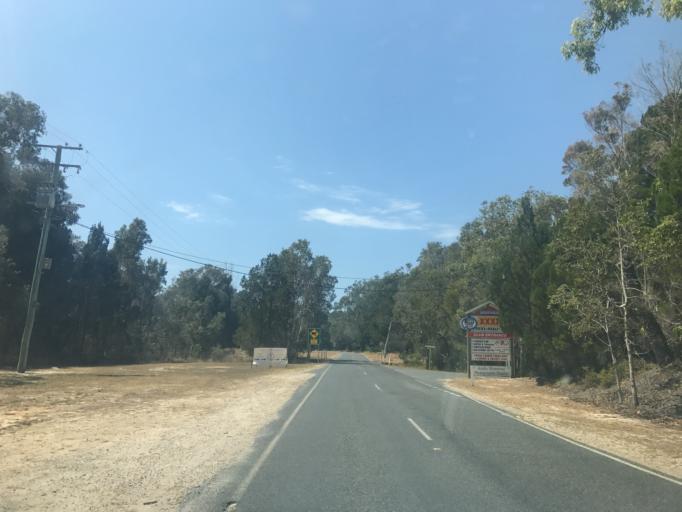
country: AU
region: Queensland
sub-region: Redland
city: Wellington Point
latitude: -27.4017
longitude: 153.4410
